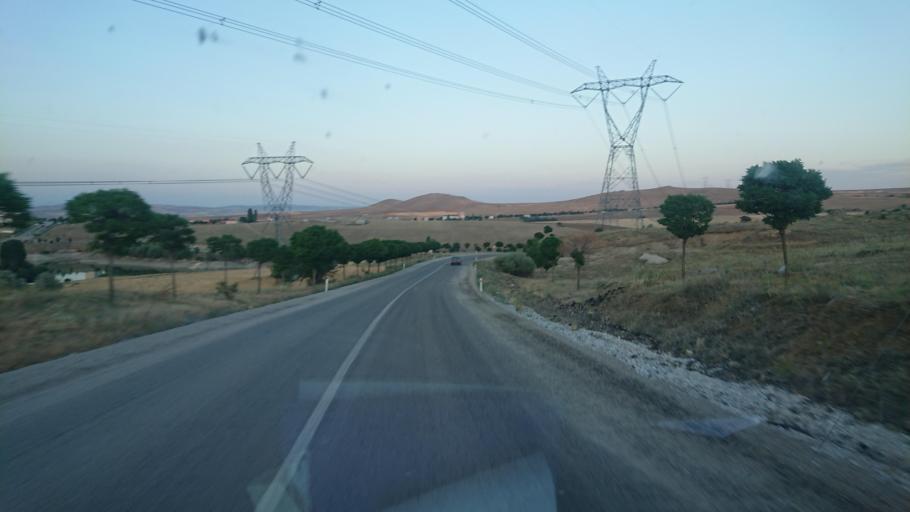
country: TR
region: Aksaray
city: Sariyahsi
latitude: 38.9705
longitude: 33.8232
